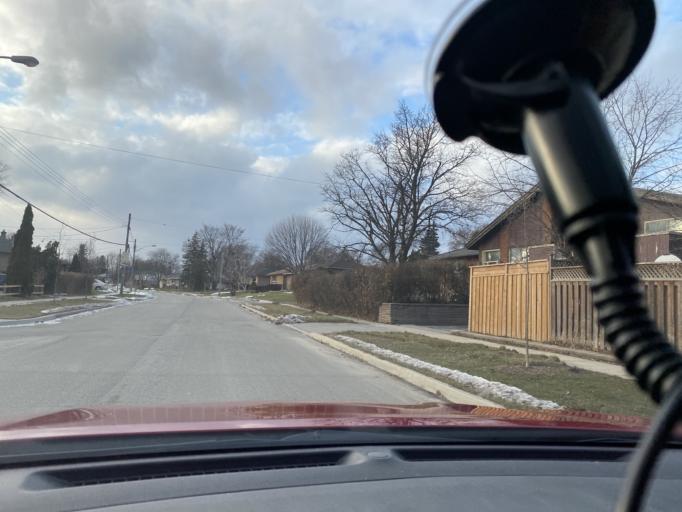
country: CA
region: Ontario
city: Scarborough
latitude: 43.7686
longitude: -79.2118
